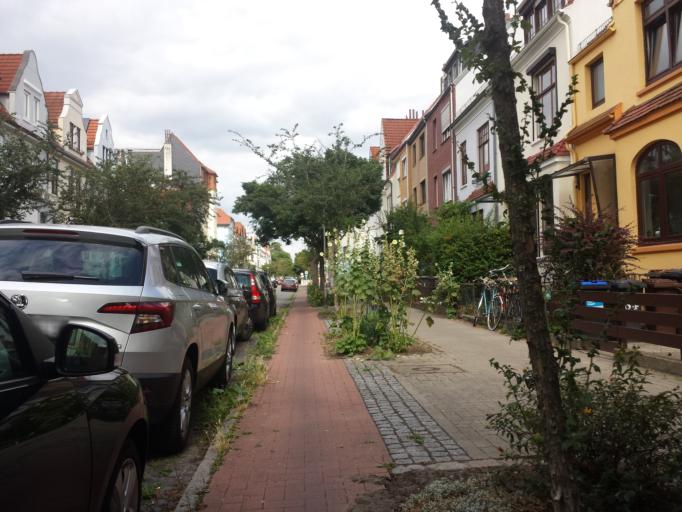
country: DE
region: Bremen
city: Bremen
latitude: 53.0671
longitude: 8.7898
